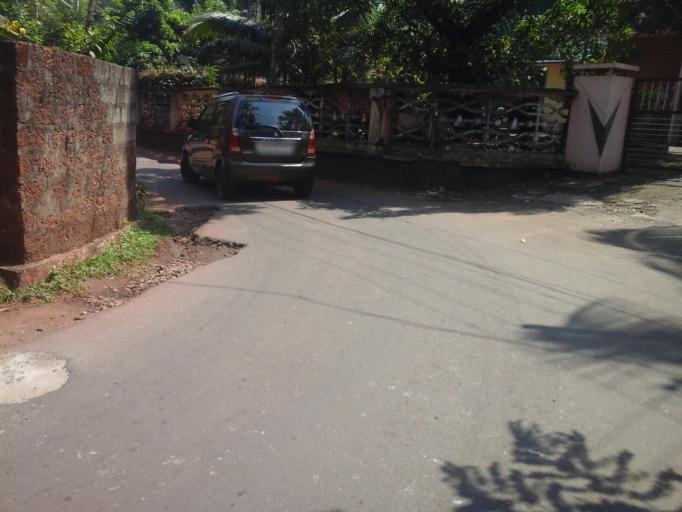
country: IN
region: Kerala
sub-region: Kannur
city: Cannanore
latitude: 11.8758
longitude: 75.3875
